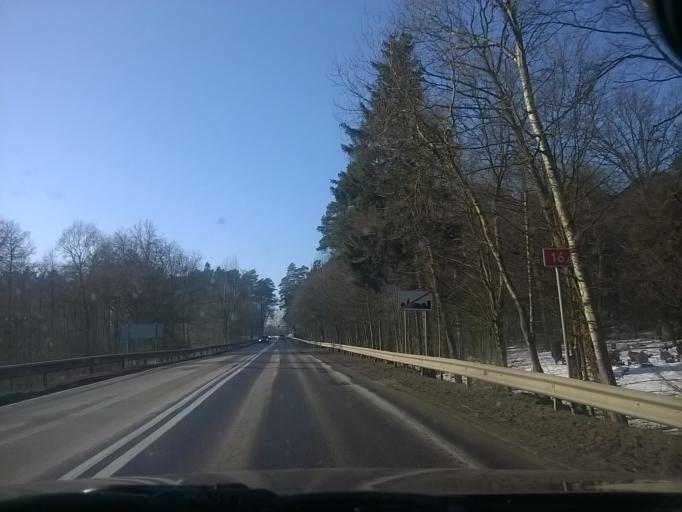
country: PL
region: Warmian-Masurian Voivodeship
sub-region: Powiat mragowski
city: Mragowo
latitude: 53.8452
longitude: 21.1395
